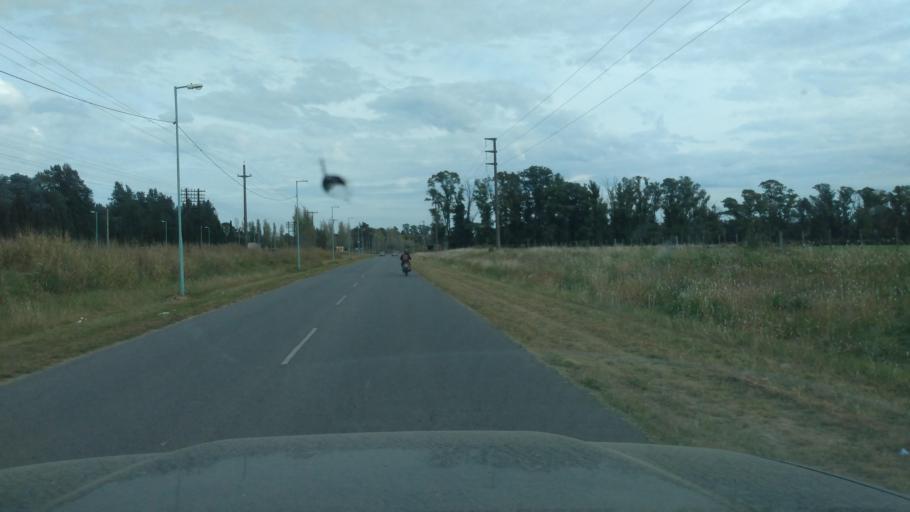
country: AR
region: Buenos Aires
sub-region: Partido de Lujan
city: Lujan
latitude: -34.5920
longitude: -59.1469
